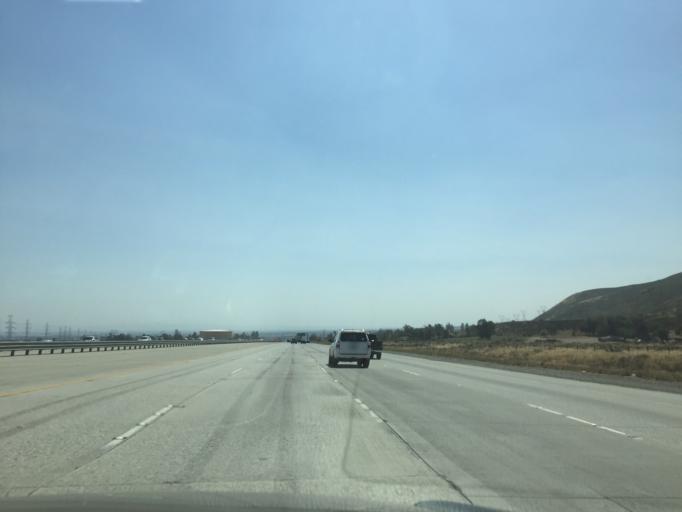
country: US
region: California
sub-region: San Bernardino County
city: Fontana
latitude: 34.1764
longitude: -117.4445
